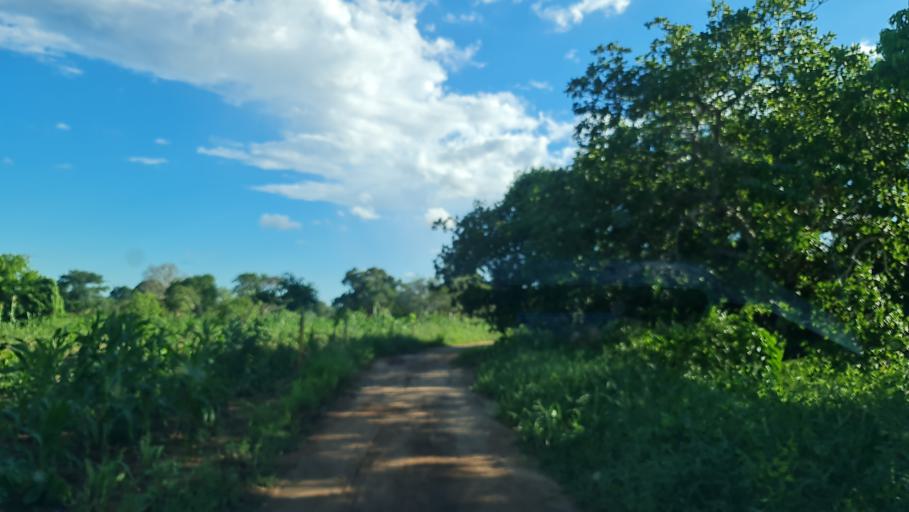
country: MZ
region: Nampula
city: Ilha de Mocambique
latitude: -14.9294
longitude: 40.2203
